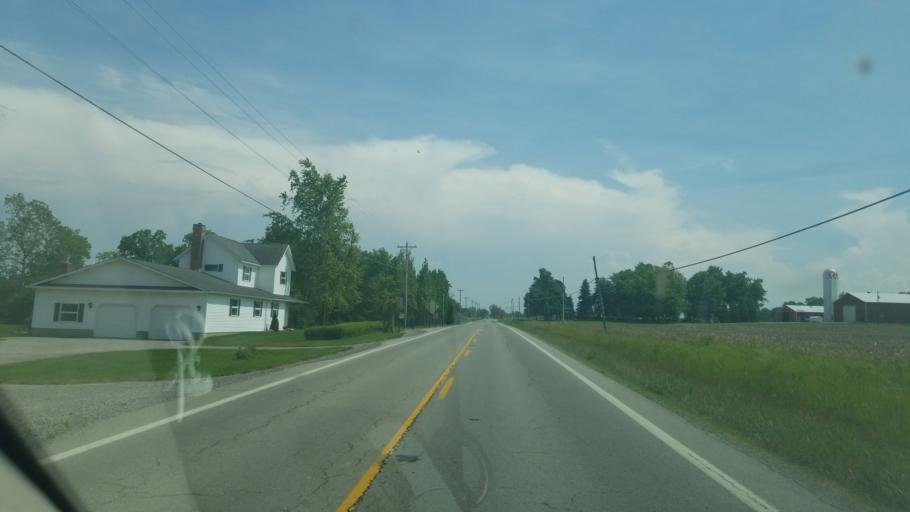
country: US
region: Ohio
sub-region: Logan County
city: Northwood
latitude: 40.4844
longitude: -83.7405
